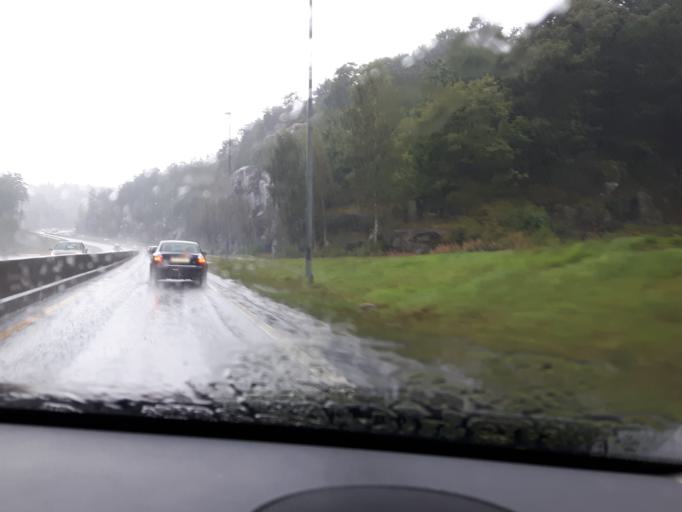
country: NO
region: Vest-Agder
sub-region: Kristiansand
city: Strai
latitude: 58.1448
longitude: 7.9123
